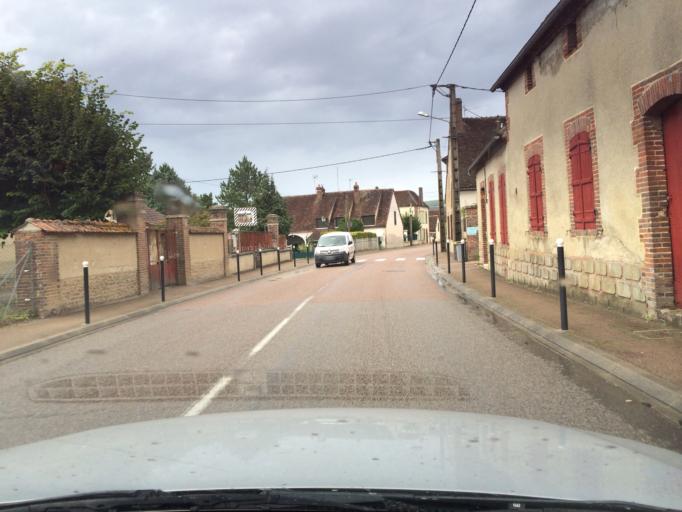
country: FR
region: Bourgogne
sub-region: Departement de l'Yonne
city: Aillant-sur-Tholon
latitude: 47.9137
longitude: 3.3599
